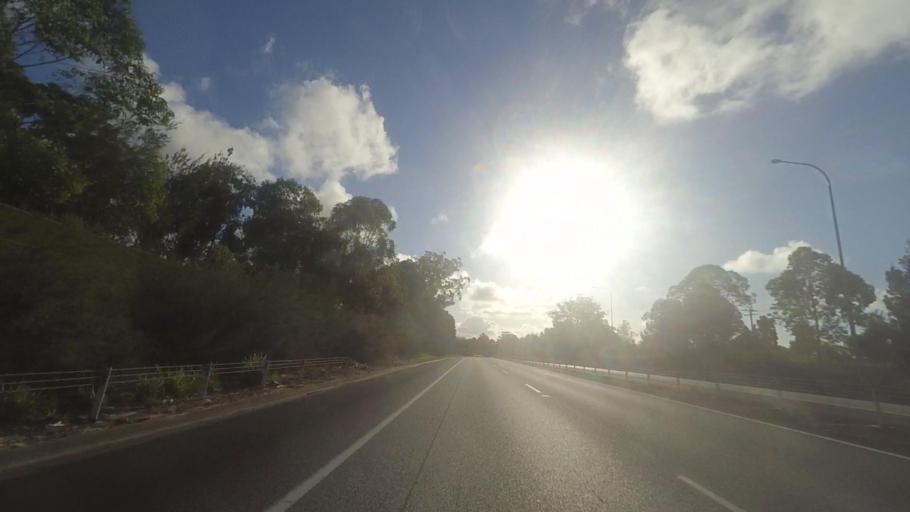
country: AU
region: New South Wales
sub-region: Great Lakes
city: Nabiac
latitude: -32.0950
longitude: 152.3812
